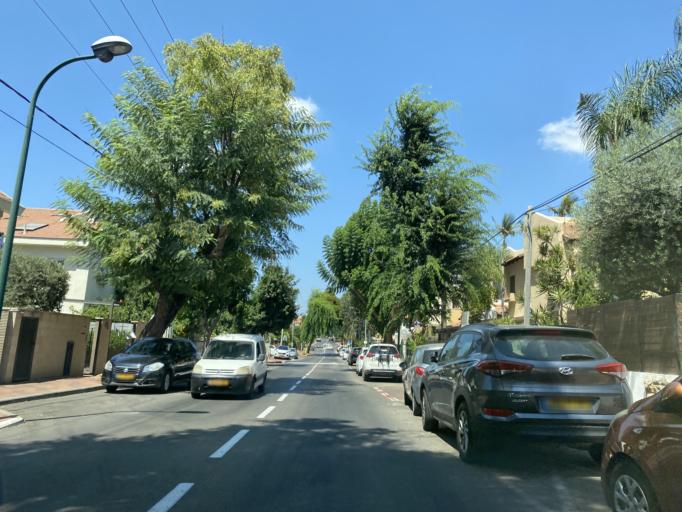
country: IL
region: Central District
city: Ra'anana
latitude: 32.1821
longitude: 34.8856
